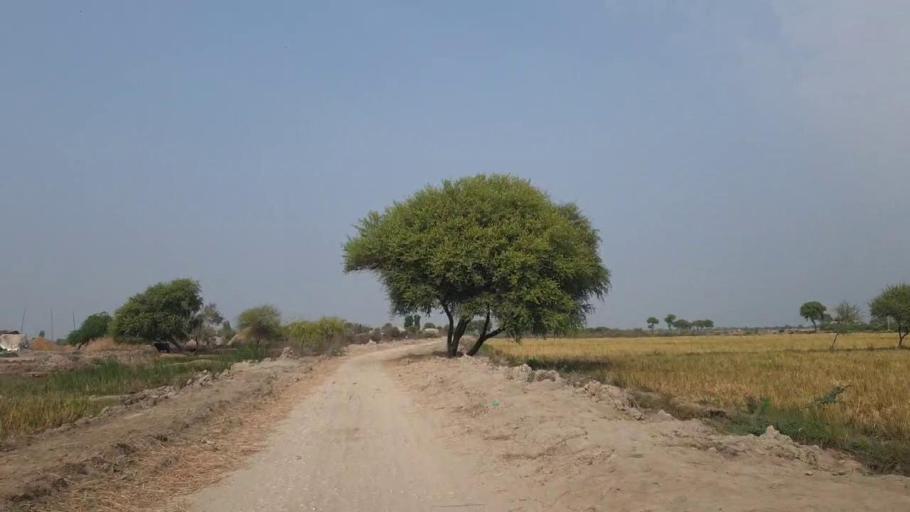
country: PK
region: Sindh
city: Badin
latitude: 24.6152
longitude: 68.7410
